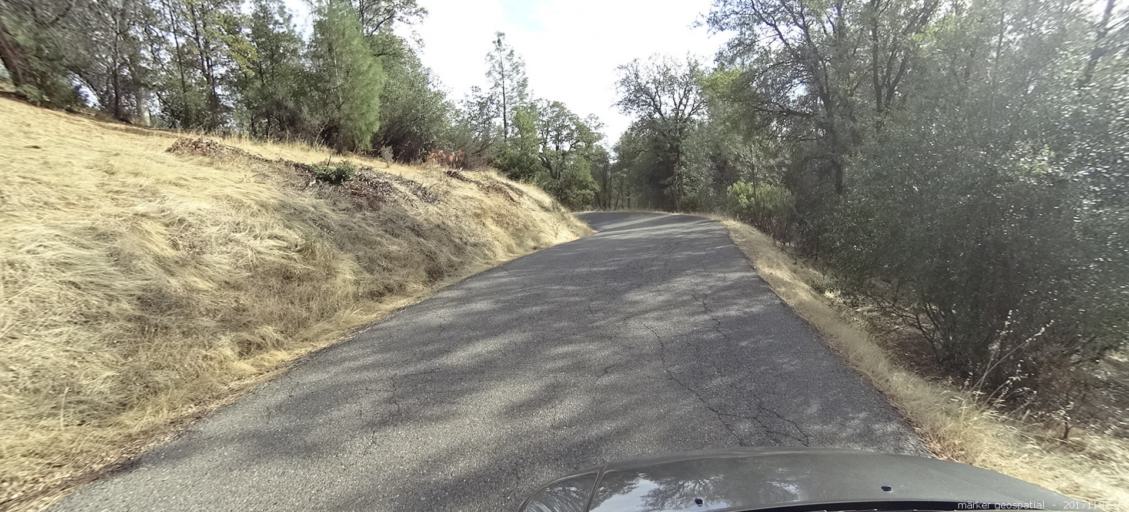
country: US
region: California
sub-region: Shasta County
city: Shasta
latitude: 40.5221
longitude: -122.5271
